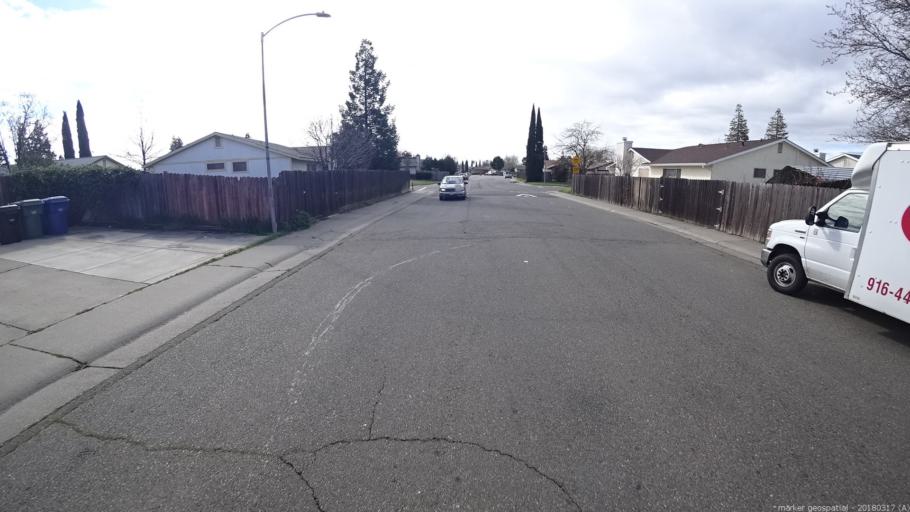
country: US
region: California
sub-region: Sacramento County
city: Florin
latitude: 38.4704
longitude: -121.3969
